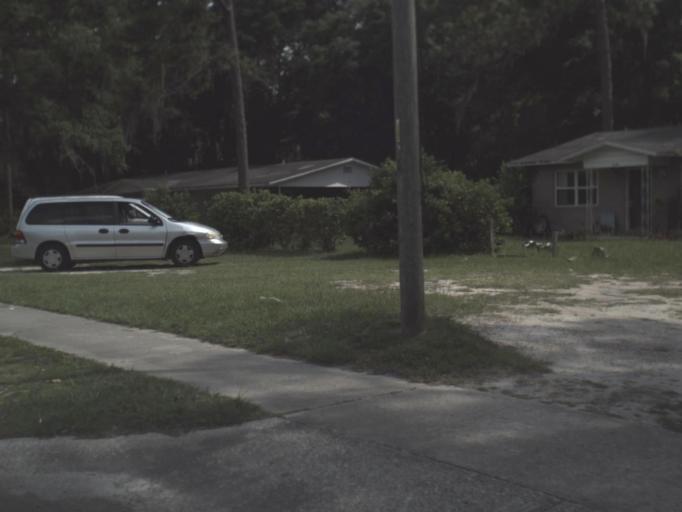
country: US
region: Florida
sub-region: Alachua County
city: Gainesville
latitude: 29.6919
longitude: -82.3328
